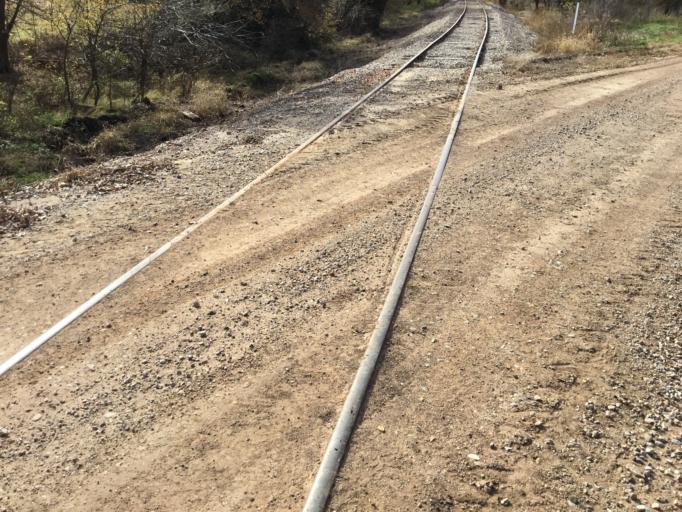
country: US
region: Kansas
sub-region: Lincoln County
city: Lincoln
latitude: 38.9146
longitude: -97.9695
